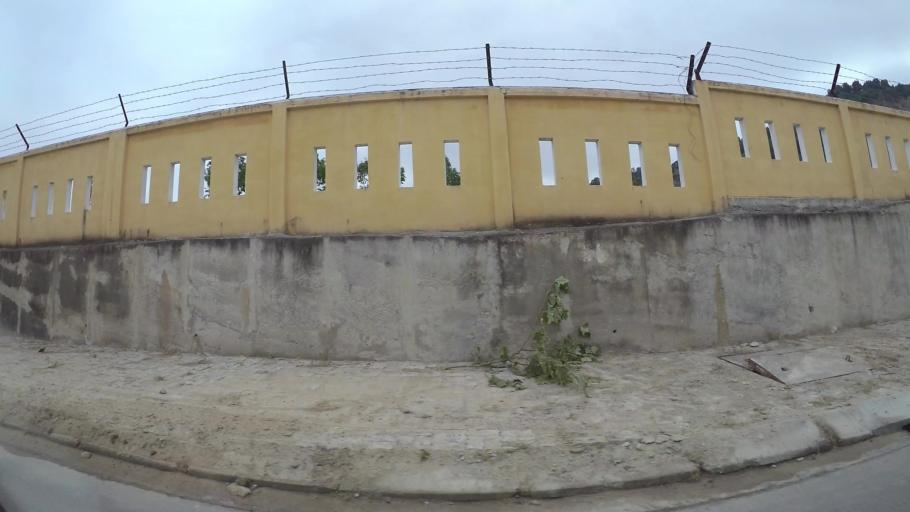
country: VN
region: Da Nang
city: Lien Chieu
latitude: 16.0434
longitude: 108.1642
